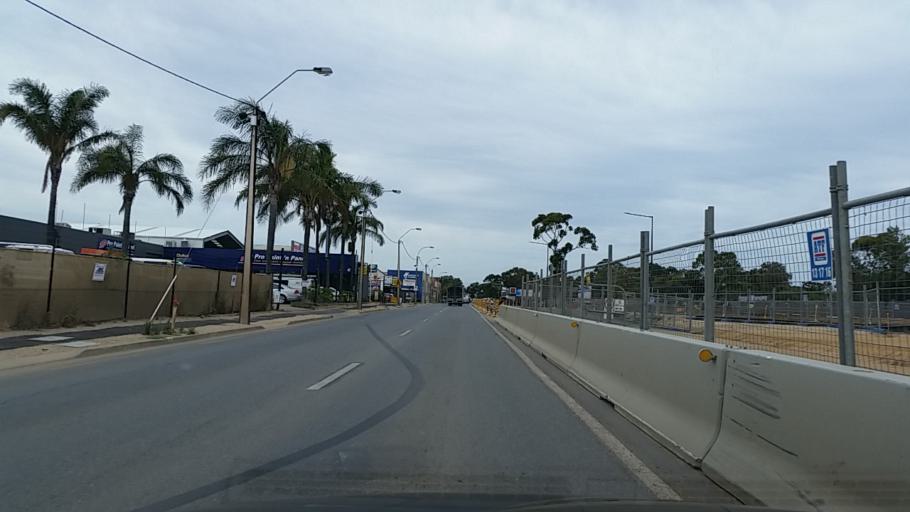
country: AU
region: South Australia
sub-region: City of West Torrens
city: Thebarton
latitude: -34.9079
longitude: 138.5653
